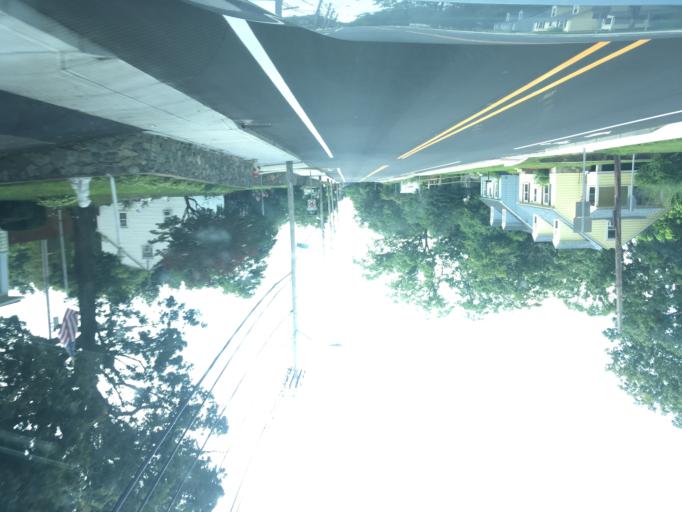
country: US
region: Rhode Island
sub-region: Kent County
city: West Warwick
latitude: 41.6825
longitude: -71.5589
